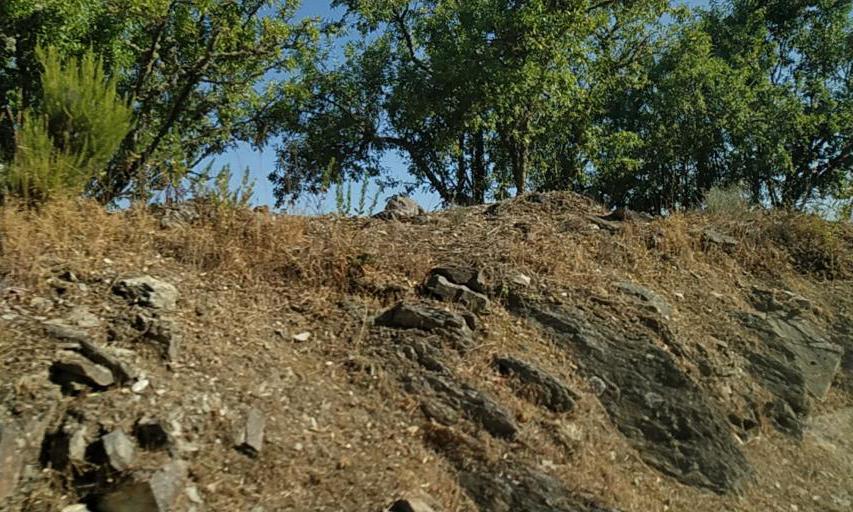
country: PT
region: Viseu
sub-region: Sao Joao da Pesqueira
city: Sao Joao da Pesqueira
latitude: 41.1613
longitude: -7.4341
